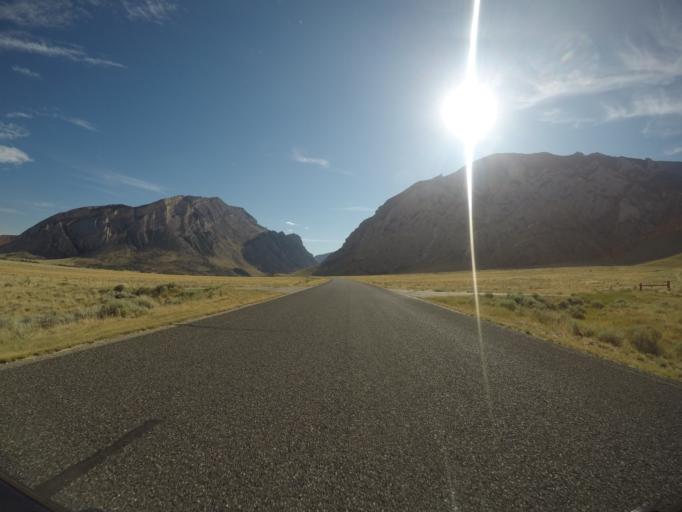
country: US
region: Montana
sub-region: Carbon County
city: Red Lodge
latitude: 44.8625
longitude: -109.2866
